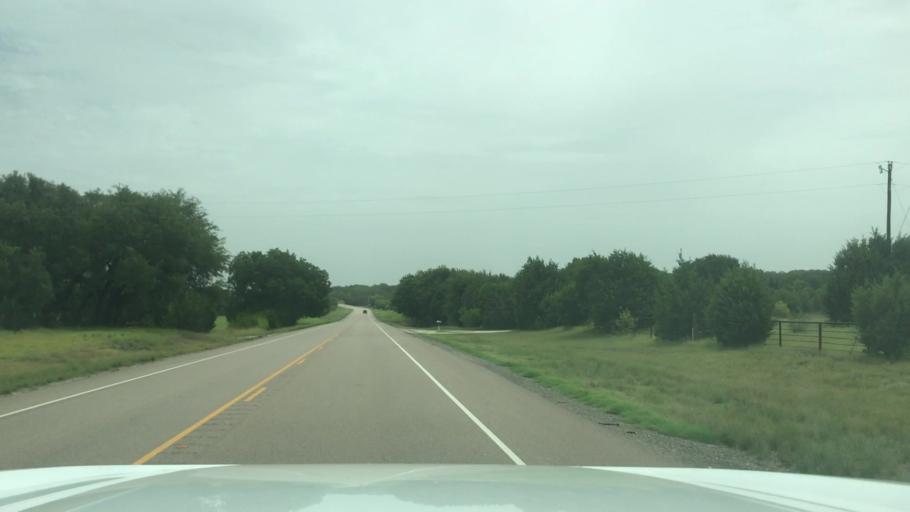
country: US
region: Texas
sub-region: Hamilton County
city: Hico
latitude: 31.9774
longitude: -97.8891
